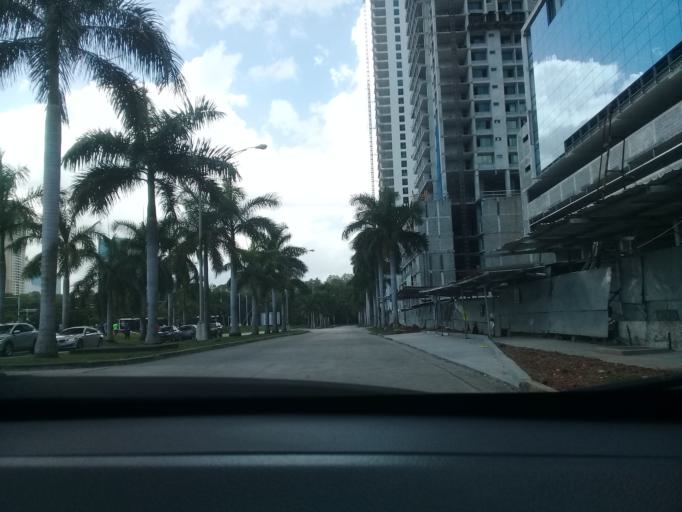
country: PA
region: Panama
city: San Miguelito
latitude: 9.0158
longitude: -79.4668
